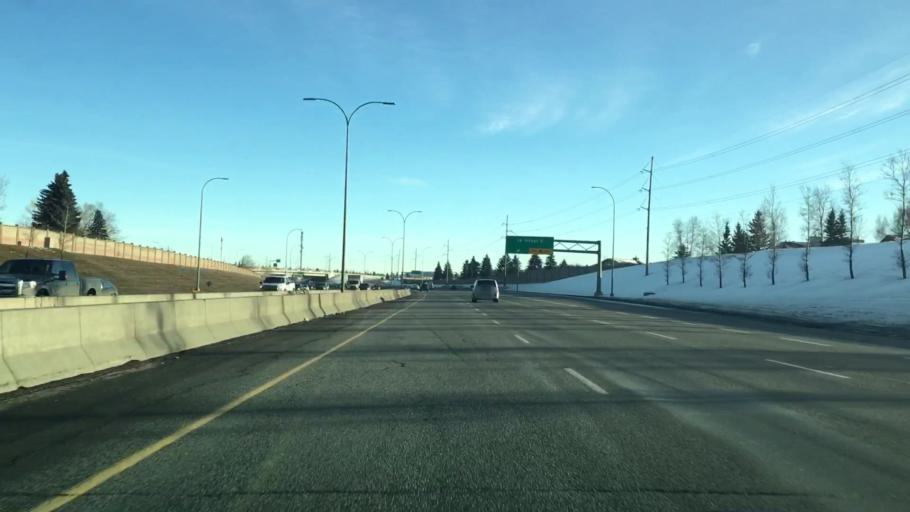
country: CA
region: Alberta
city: Calgary
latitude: 50.9842
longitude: -114.0219
